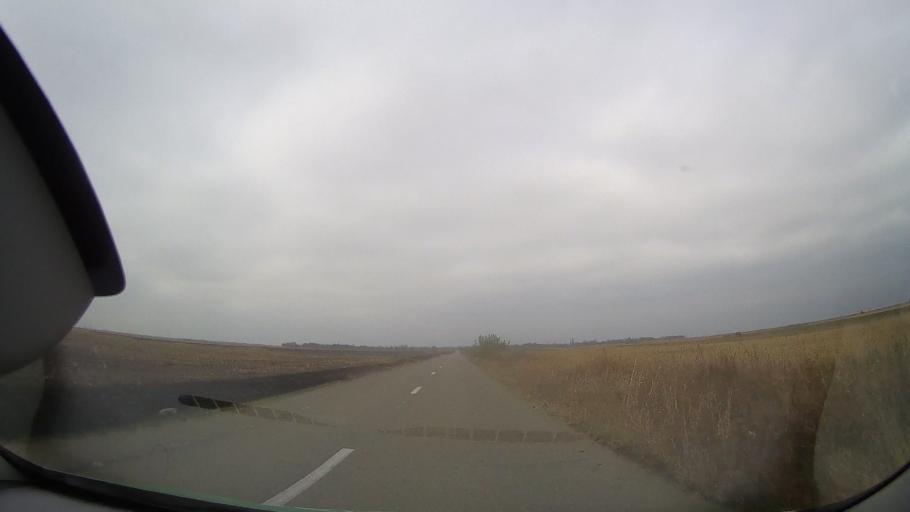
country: RO
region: Buzau
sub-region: Comuna Scutelnici
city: Scutelnici
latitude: 44.8654
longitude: 26.8948
